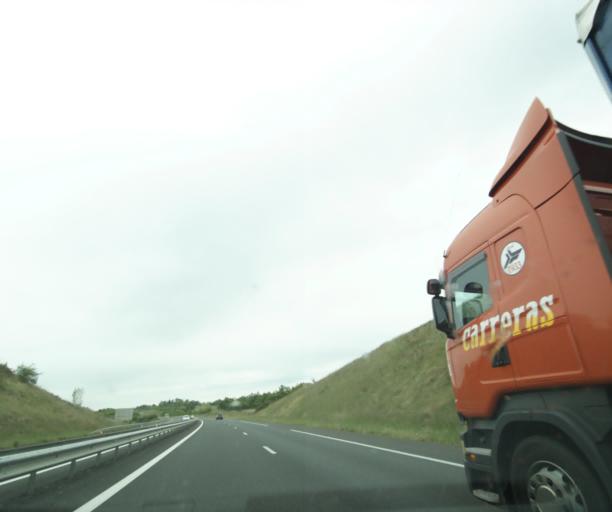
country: FR
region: Midi-Pyrenees
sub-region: Departement du Lot
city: Cahors
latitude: 44.5526
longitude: 1.5173
